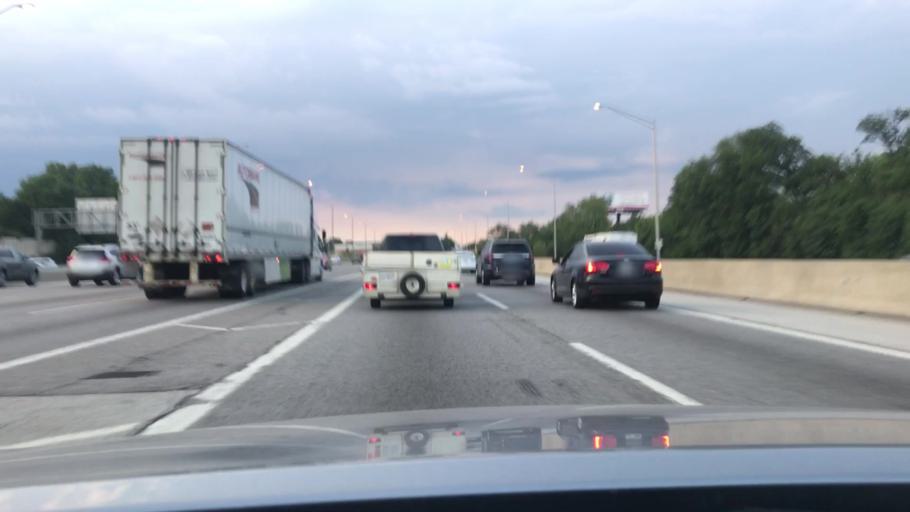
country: US
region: Illinois
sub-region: Cook County
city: Indian Head Park
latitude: 41.7771
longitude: -87.9075
